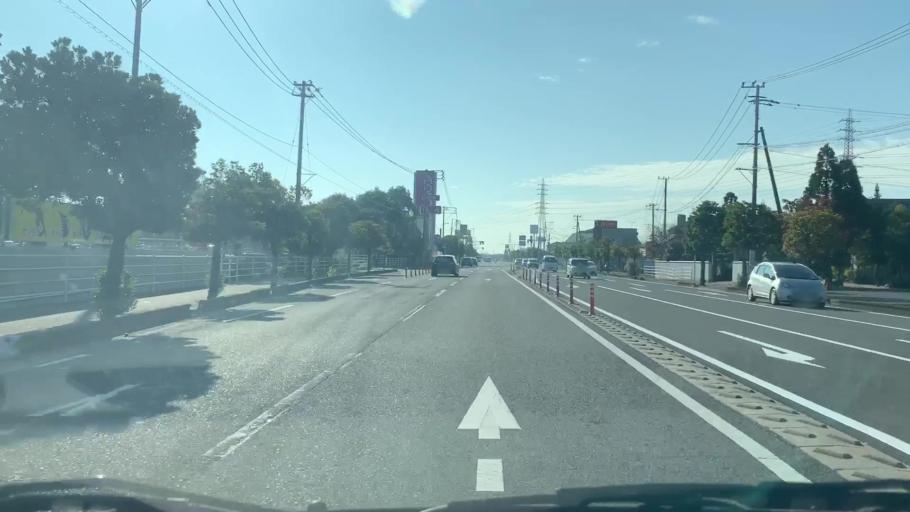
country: JP
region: Saga Prefecture
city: Saga-shi
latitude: 33.3045
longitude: 130.2786
